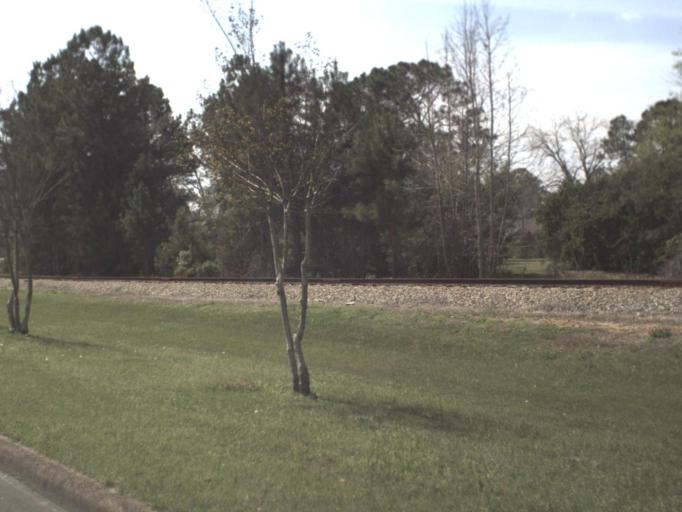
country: US
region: Florida
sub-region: Gadsden County
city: Havana
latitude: 30.6296
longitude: -84.4151
